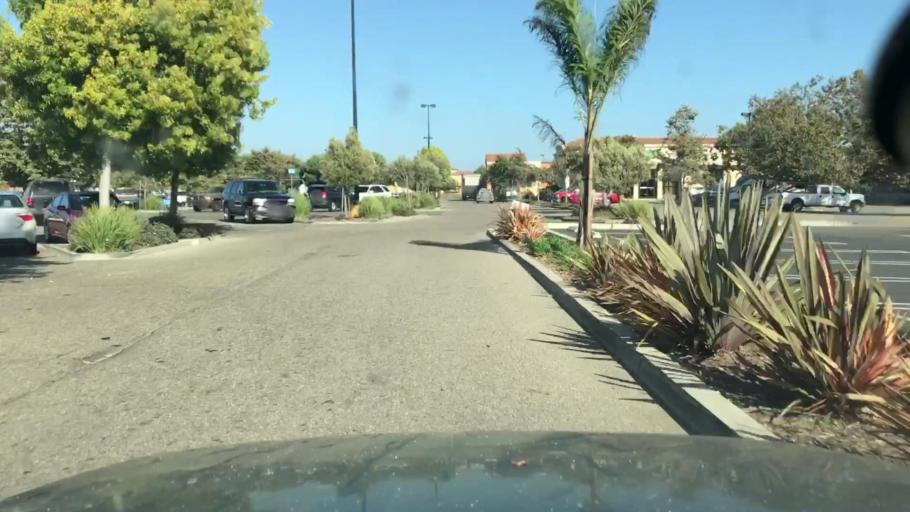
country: US
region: California
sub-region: Santa Barbara County
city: Lompoc
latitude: 34.6615
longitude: -120.4659
